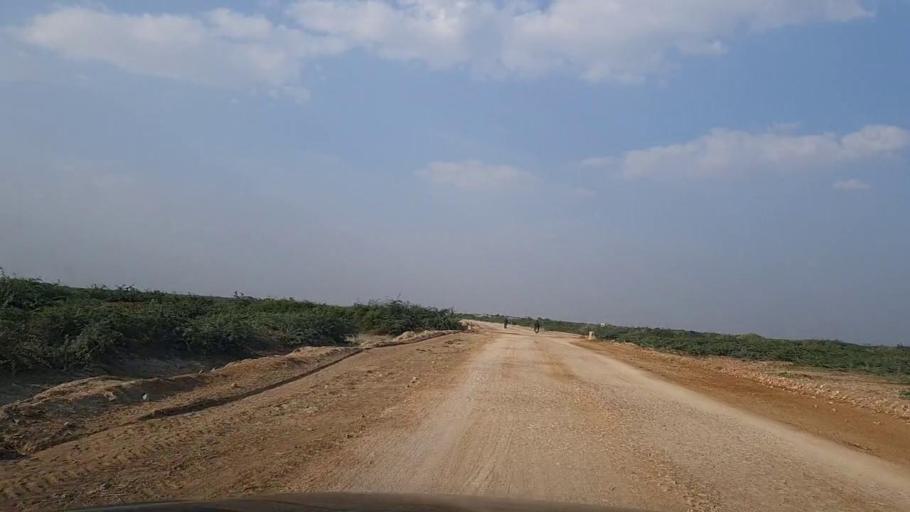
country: PK
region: Sindh
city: Gharo
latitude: 24.7936
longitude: 67.7448
